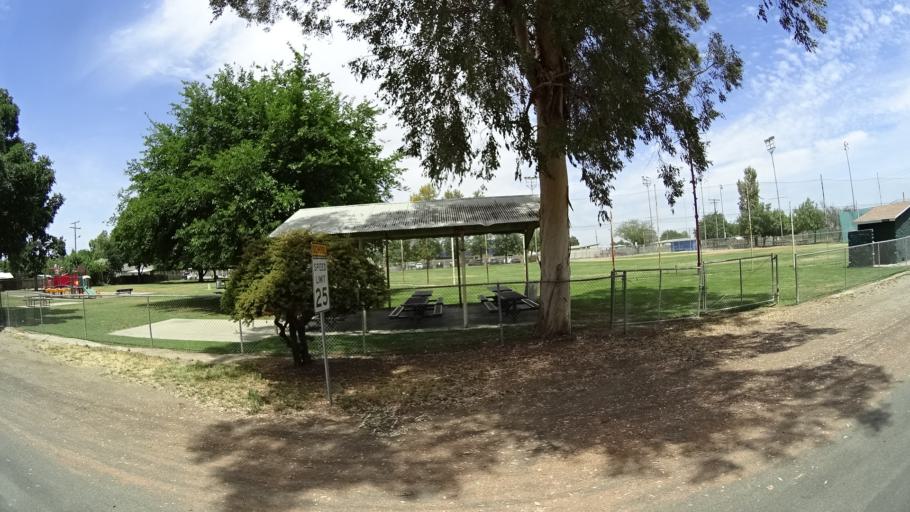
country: US
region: California
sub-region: Kings County
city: Armona
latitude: 36.3103
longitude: -119.7070
